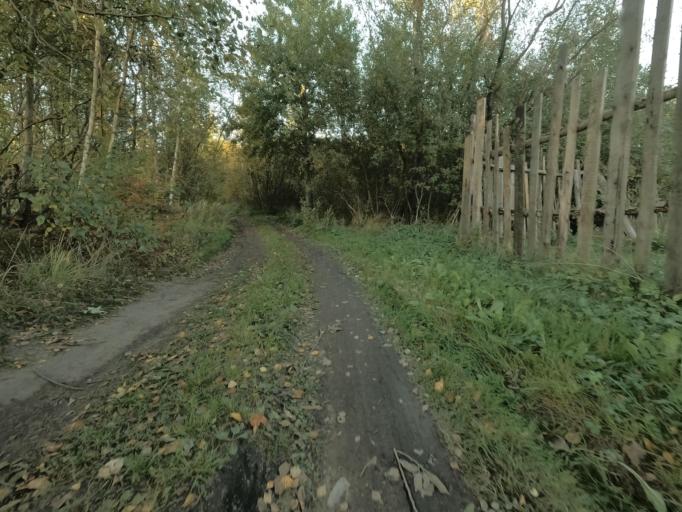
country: RU
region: Leningrad
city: Nikol'skoye
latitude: 59.7131
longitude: 30.7978
